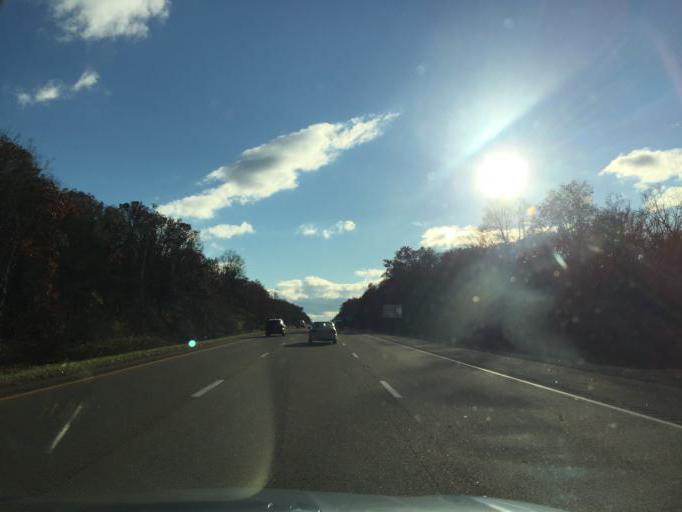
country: US
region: Massachusetts
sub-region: Bristol County
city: North Seekonk
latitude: 41.9253
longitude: -71.3271
